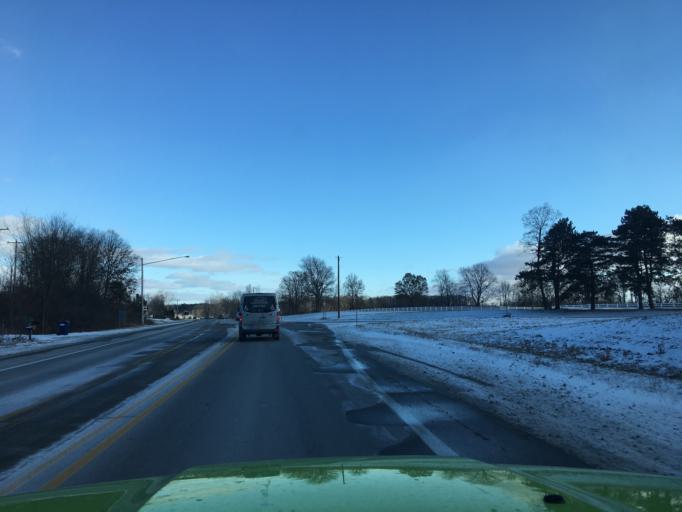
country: US
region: Michigan
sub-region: Kent County
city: Cedar Springs
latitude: 43.1762
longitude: -85.5331
